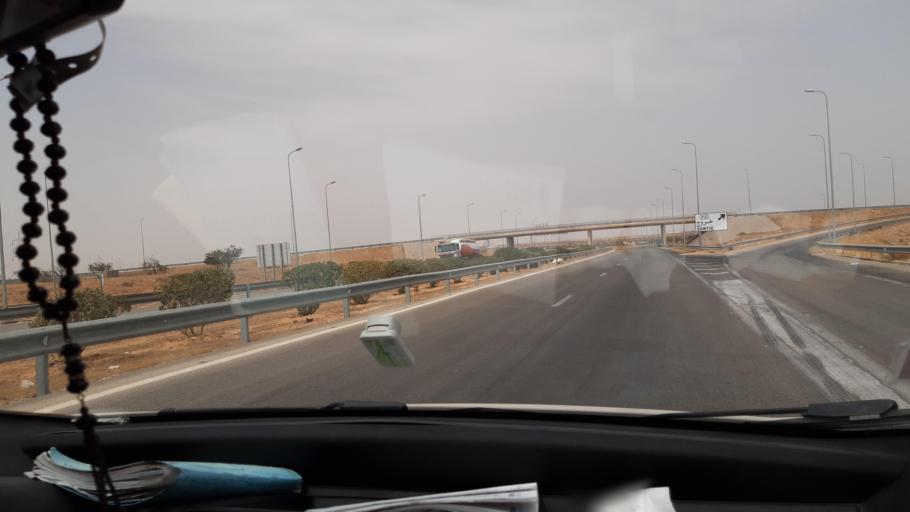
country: TN
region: Safaqis
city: Sfax
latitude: 34.7263
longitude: 10.5878
